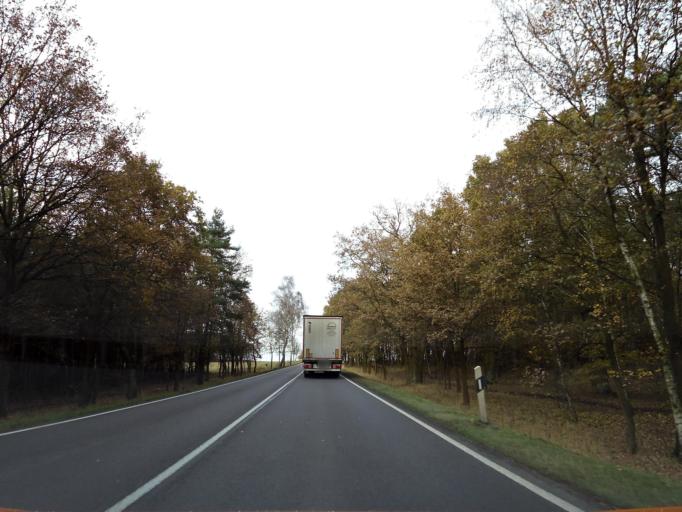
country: DE
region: Saxony-Anhalt
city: Klotze
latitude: 52.7078
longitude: 11.2520
